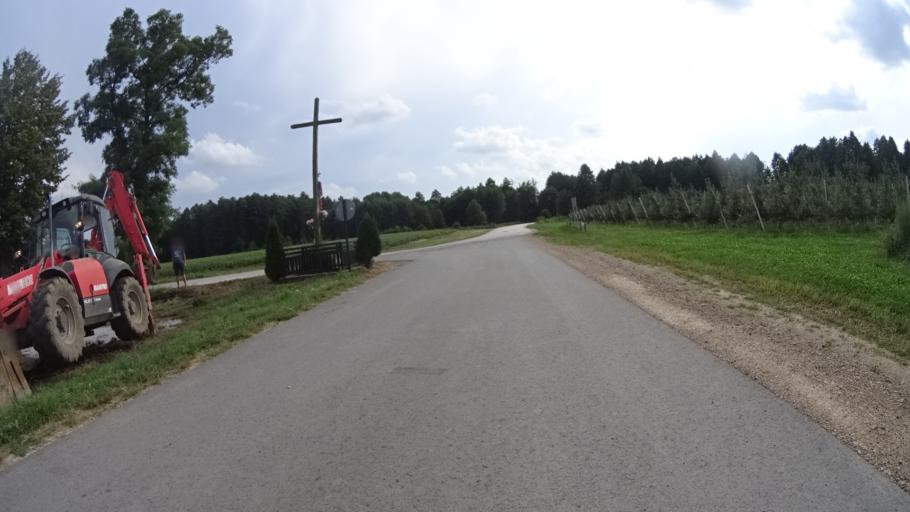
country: PL
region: Masovian Voivodeship
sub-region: Powiat grojecki
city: Goszczyn
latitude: 51.6954
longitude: 20.8217
